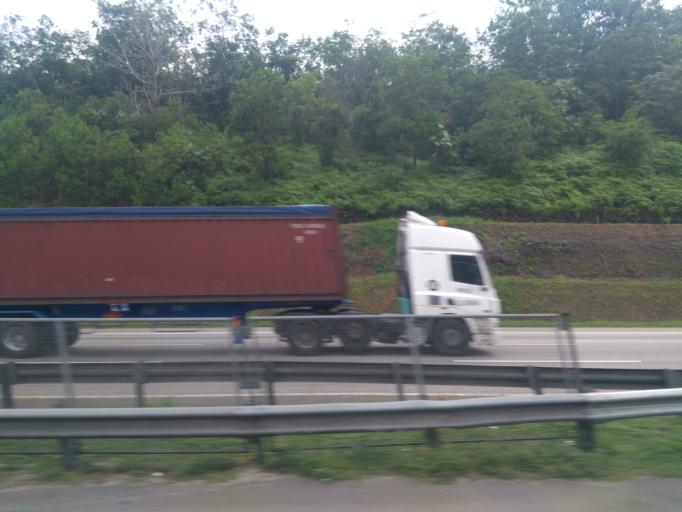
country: MY
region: Negeri Sembilan
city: Seremban
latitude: 2.6415
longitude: 101.9946
